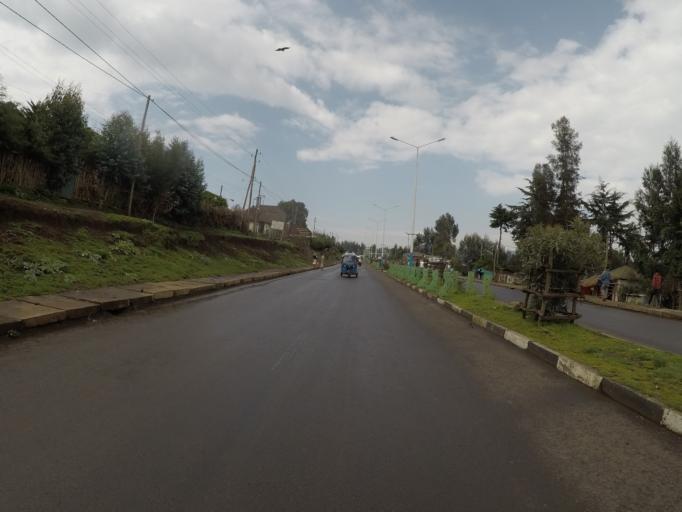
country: ET
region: Amhara
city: Debark'
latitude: 13.1486
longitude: 37.8947
